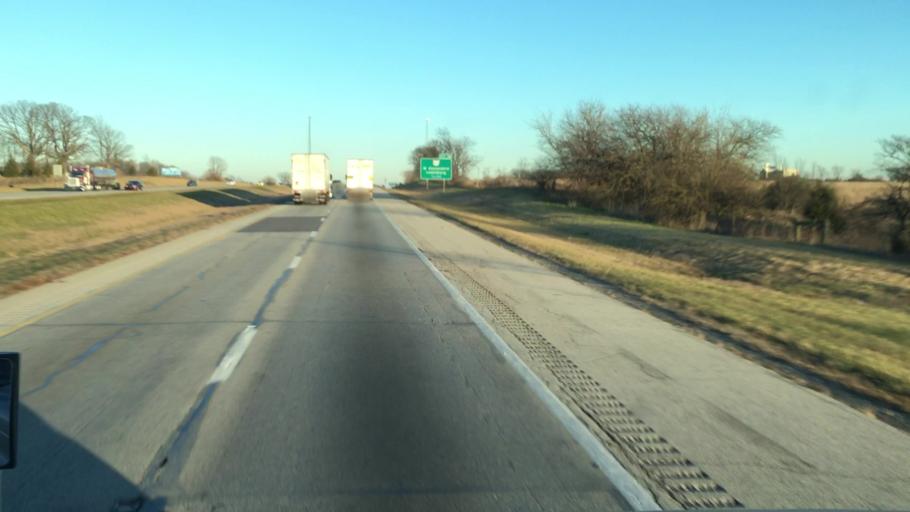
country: US
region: Ohio
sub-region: Preble County
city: Lewisburg
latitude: 39.8369
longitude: -84.5553
